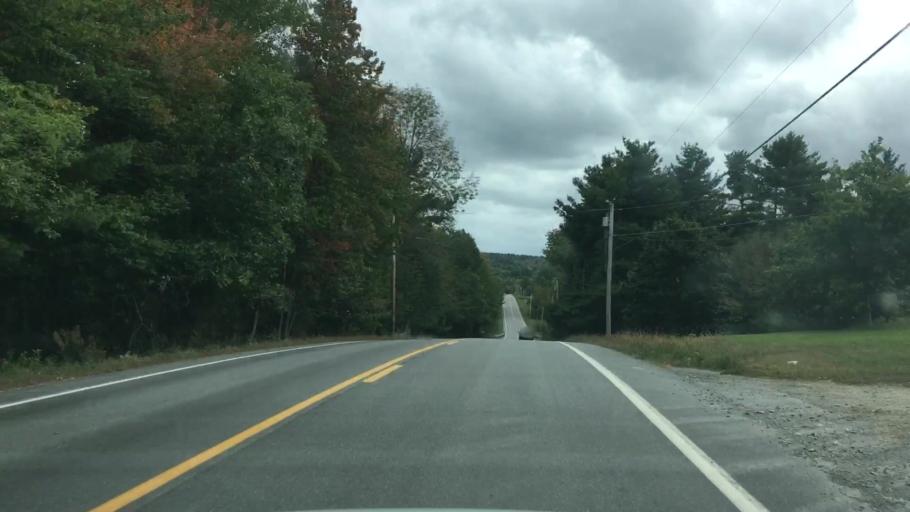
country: US
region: Maine
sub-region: Penobscot County
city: Hermon
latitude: 44.7531
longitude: -68.9715
